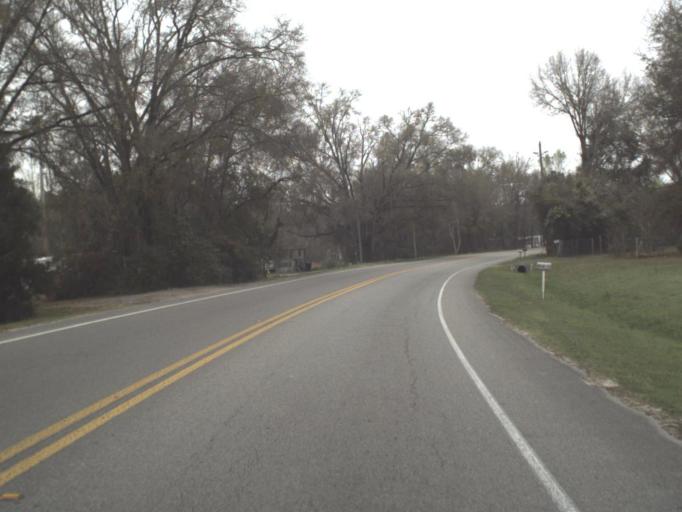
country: US
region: Florida
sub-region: Liberty County
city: Bristol
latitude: 30.3822
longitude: -84.7984
